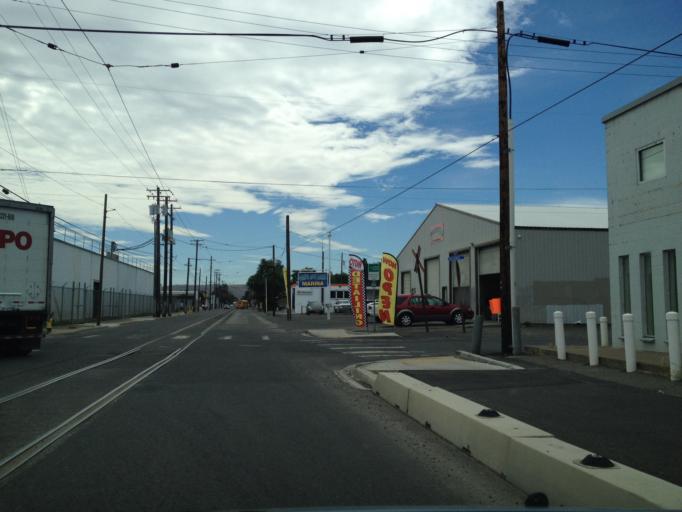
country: US
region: Washington
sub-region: Yakima County
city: Yakima
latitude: 46.6147
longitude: -120.5199
